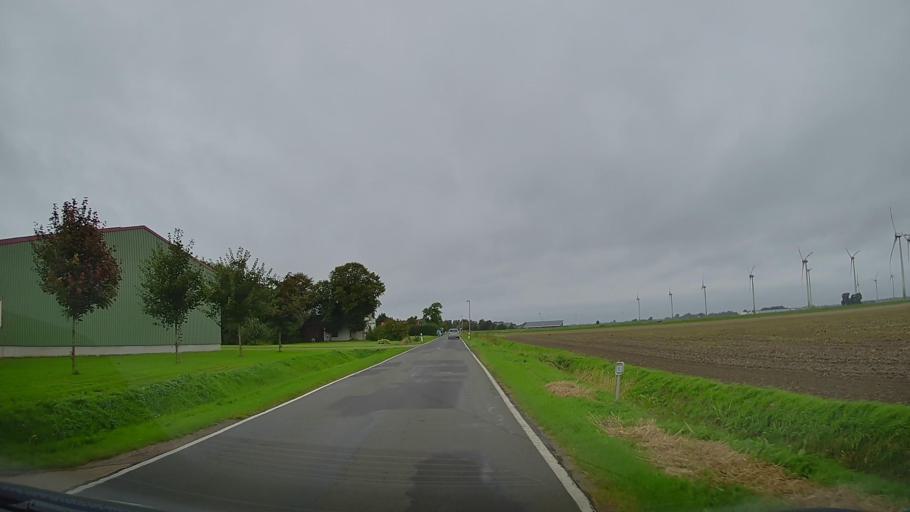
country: DE
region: Schleswig-Holstein
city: Neufeld
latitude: 53.9128
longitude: 9.0028
